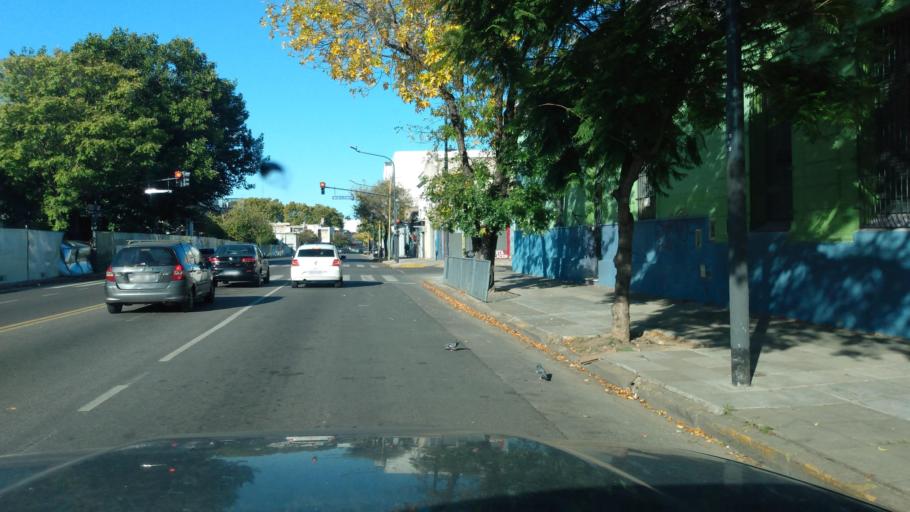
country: AR
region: Buenos Aires F.D.
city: Villa Santa Rita
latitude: -34.5966
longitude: -58.4612
